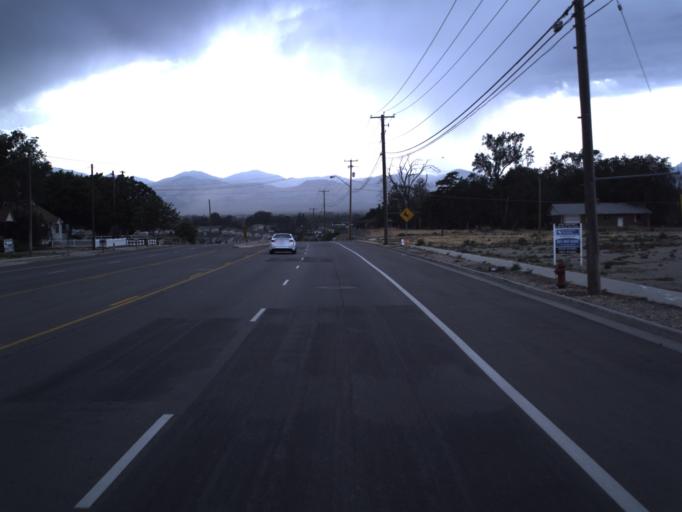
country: US
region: Utah
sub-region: Salt Lake County
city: Riverton
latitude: 40.5269
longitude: -111.9086
